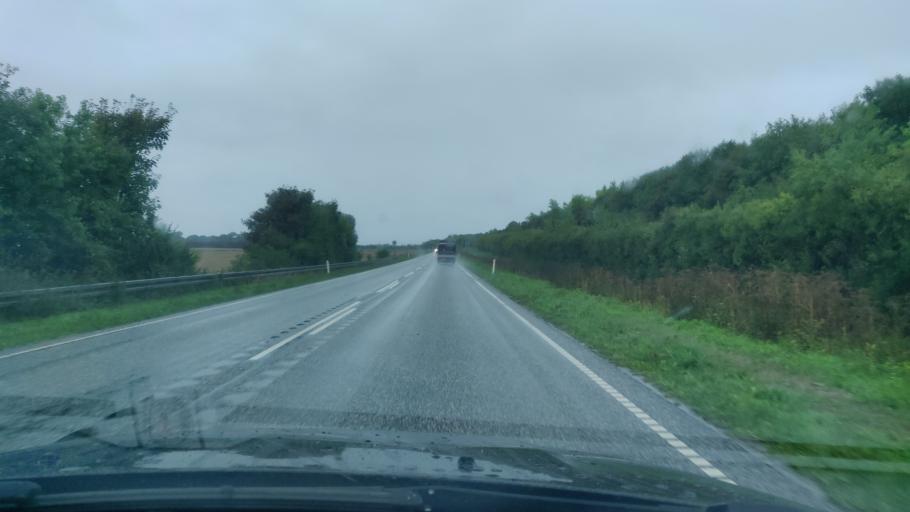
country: DK
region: North Denmark
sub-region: Thisted Kommune
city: Thisted
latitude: 56.9725
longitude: 8.7016
